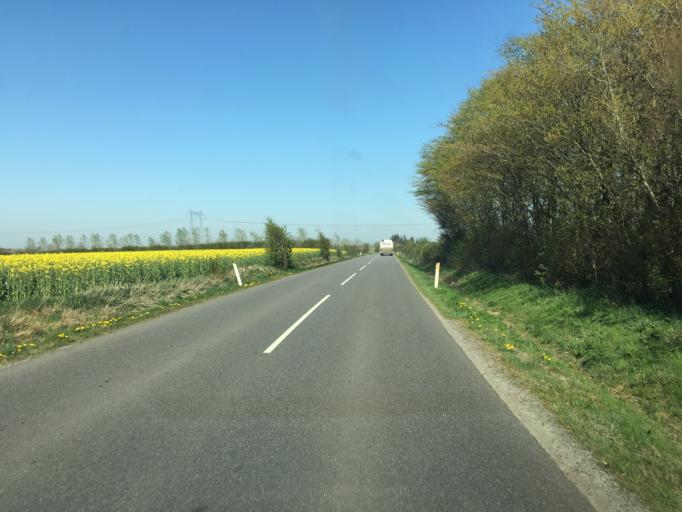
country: DK
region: South Denmark
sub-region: Aabenraa Kommune
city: Tinglev
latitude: 54.9954
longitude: 9.2951
